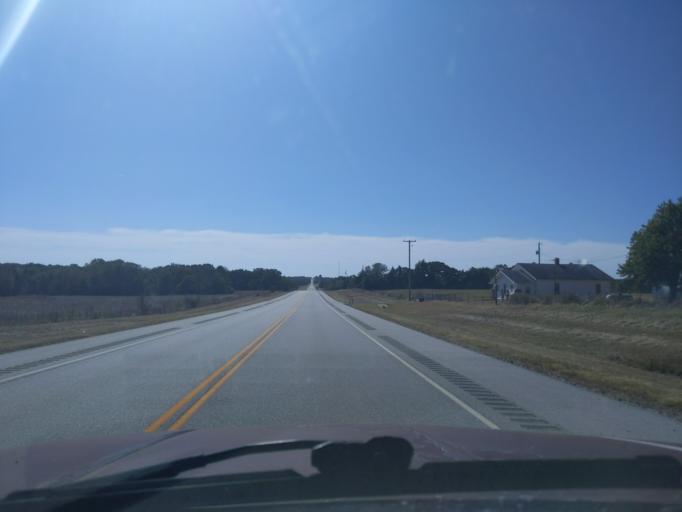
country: US
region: Oklahoma
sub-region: Creek County
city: Bristow
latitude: 35.7469
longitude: -96.3872
